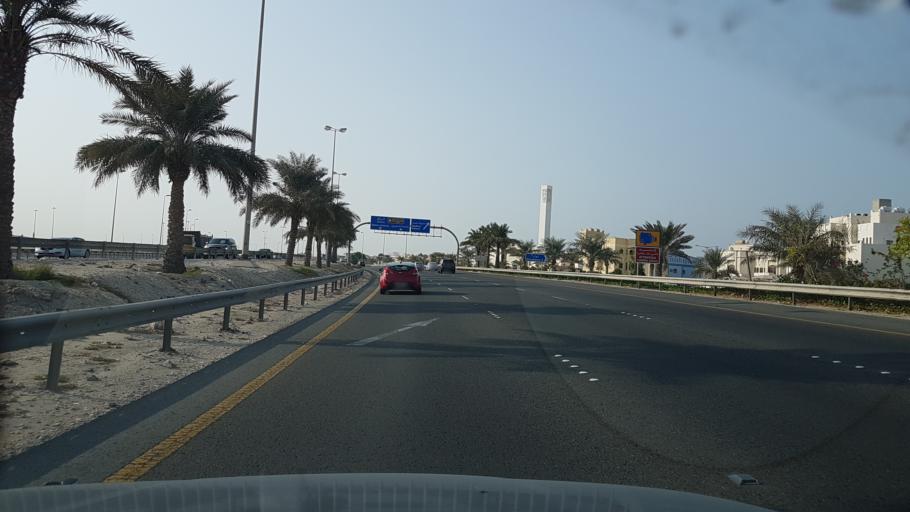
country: BH
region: Central Governorate
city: Madinat Hamad
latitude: 26.1280
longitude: 50.5064
